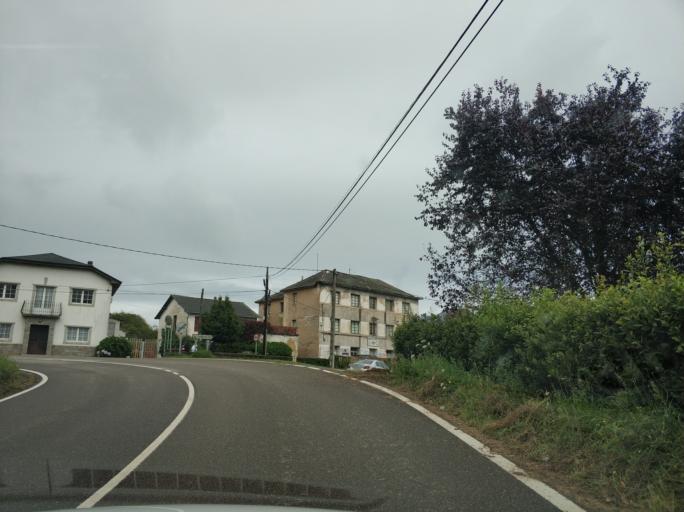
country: ES
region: Asturias
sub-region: Province of Asturias
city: Salas
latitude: 43.5459
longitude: -6.3863
